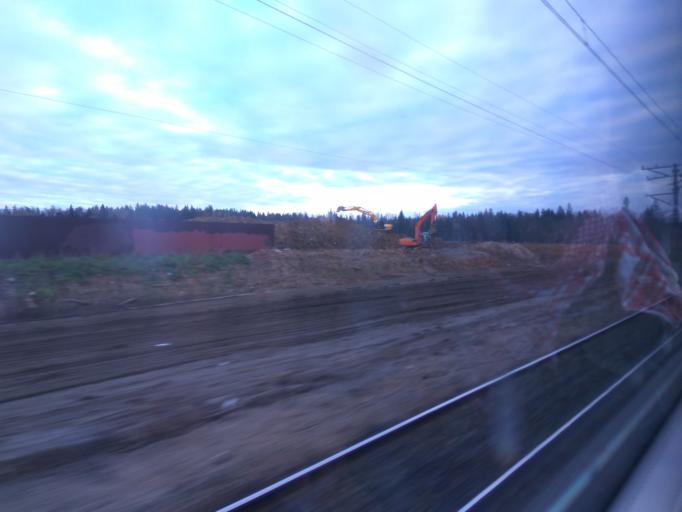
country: RU
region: Moskovskaya
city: Selyatino
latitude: 55.5127
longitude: 36.9607
